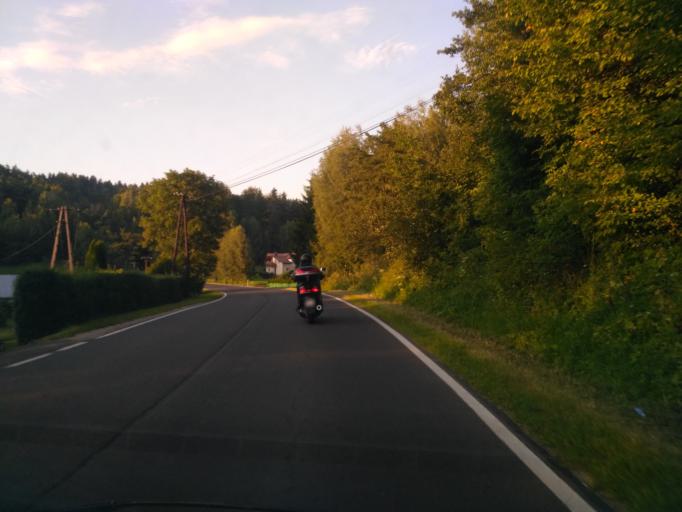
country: PL
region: Subcarpathian Voivodeship
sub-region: Powiat krosnienski
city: Korczyna
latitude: 49.7376
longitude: 21.8075
